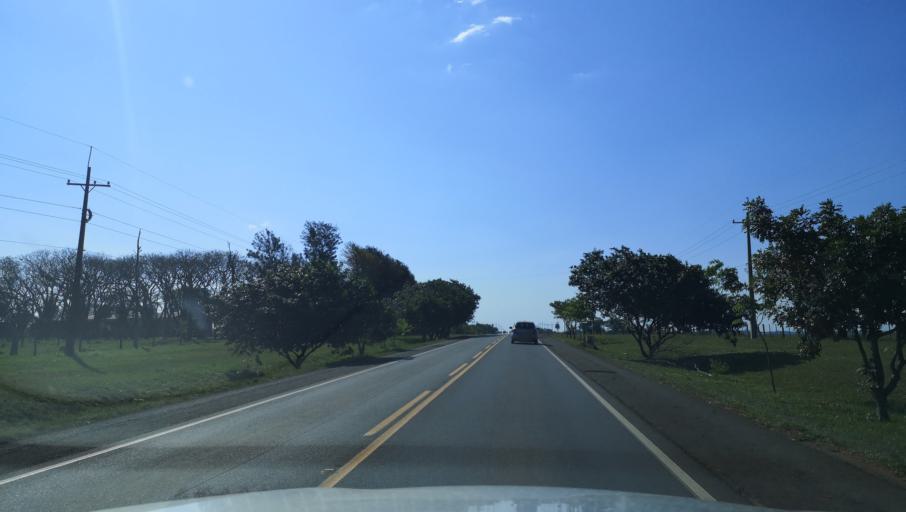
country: PY
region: Misiones
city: San Patricio
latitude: -26.9622
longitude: -56.8362
